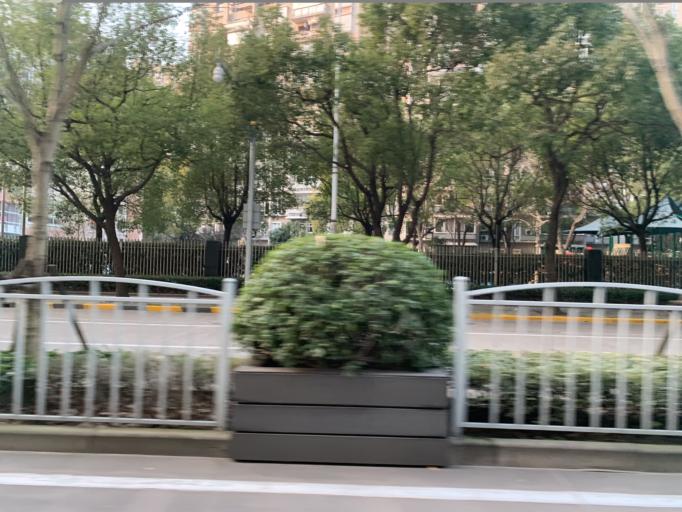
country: CN
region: Shanghai Shi
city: Huamu
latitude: 31.2287
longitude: 121.5493
